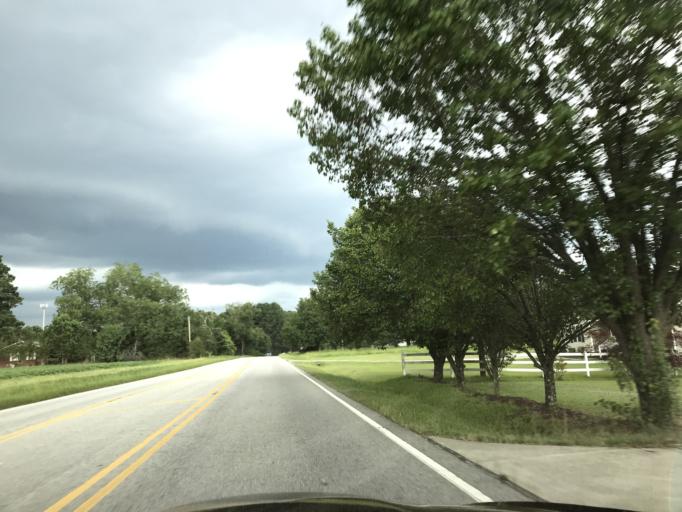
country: US
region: North Carolina
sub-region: Johnston County
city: Four Oaks
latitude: 35.5142
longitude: -78.5035
